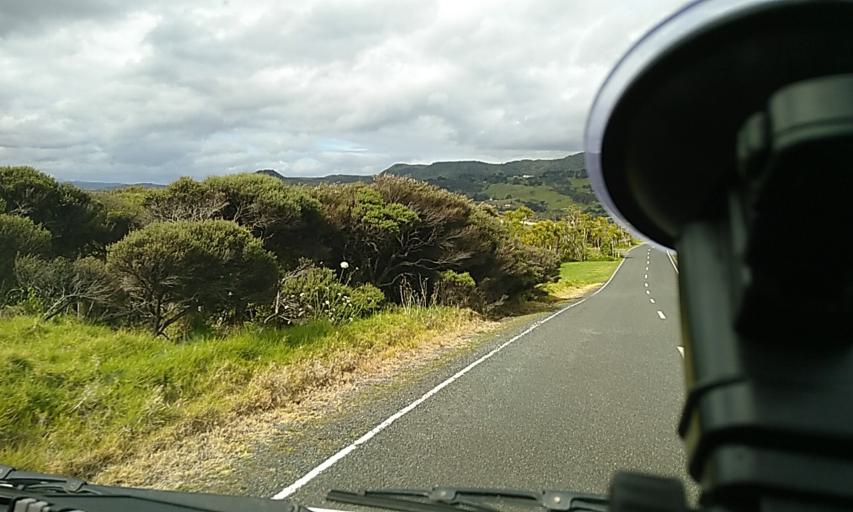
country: NZ
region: Northland
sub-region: Far North District
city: Ahipara
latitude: -35.5383
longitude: 173.3751
